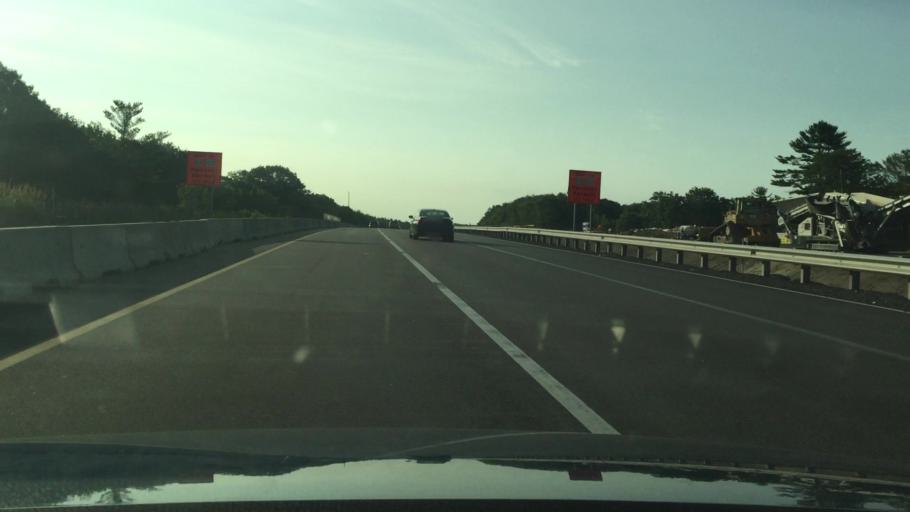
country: US
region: Massachusetts
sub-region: Plymouth County
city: Hanover
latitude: 42.1555
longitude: -70.8565
